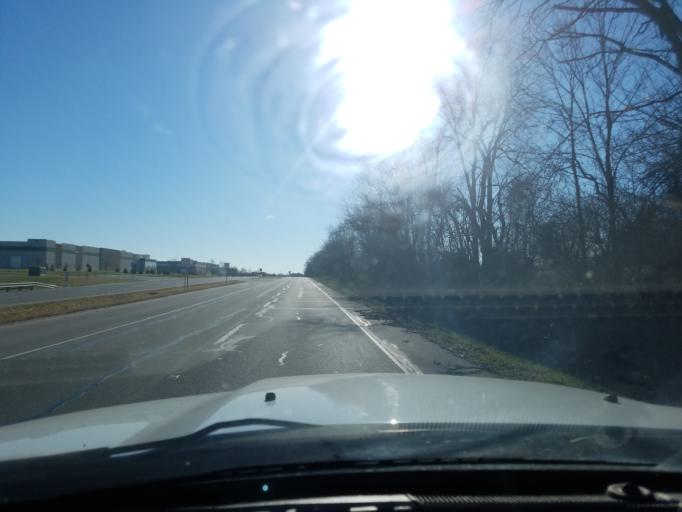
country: US
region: Indiana
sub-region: Clark County
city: Sellersburg
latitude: 38.3802
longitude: -85.6910
